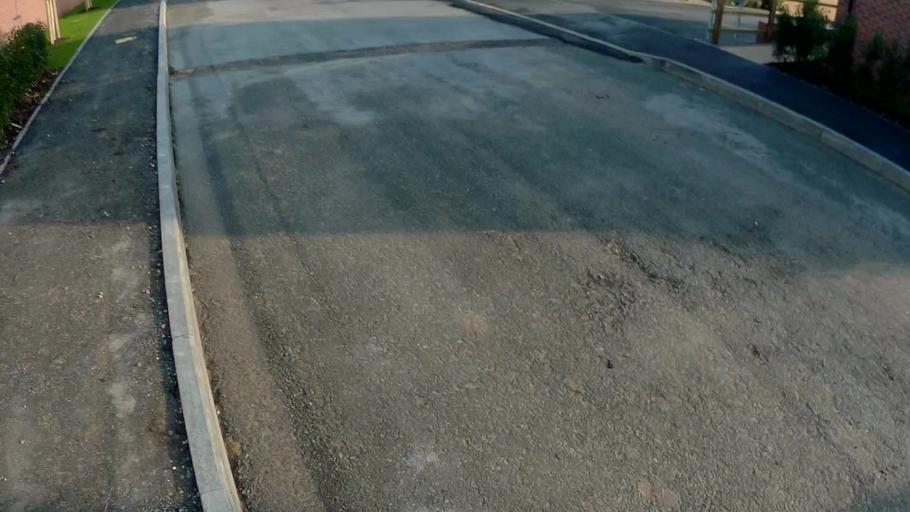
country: GB
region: England
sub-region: Lincolnshire
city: Bourne
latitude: 52.7589
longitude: -0.3883
